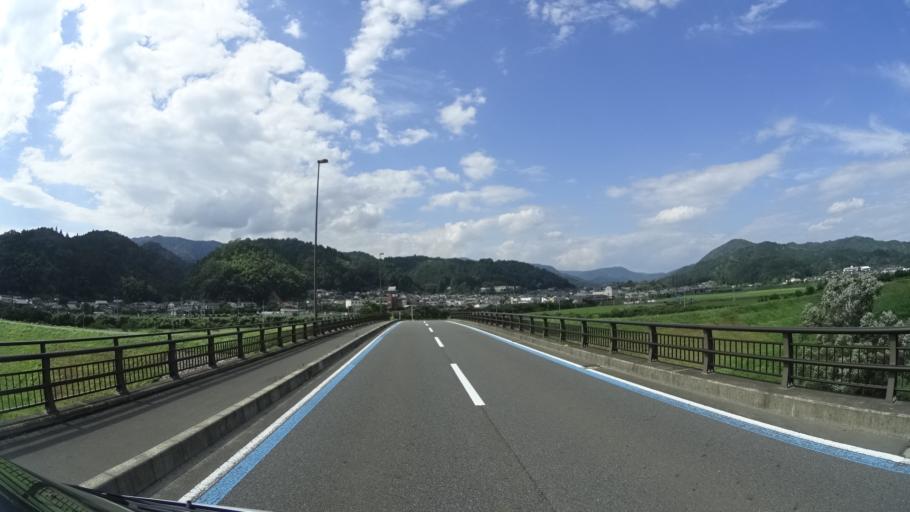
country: JP
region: Kyoto
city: Fukuchiyama
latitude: 35.3844
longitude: 135.1470
